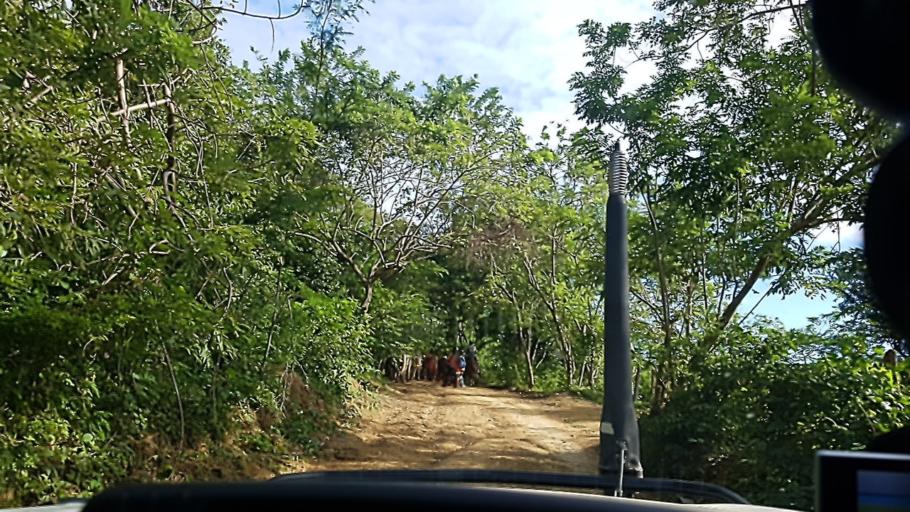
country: NI
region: Rivas
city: Tola
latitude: 11.5180
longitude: -86.1363
